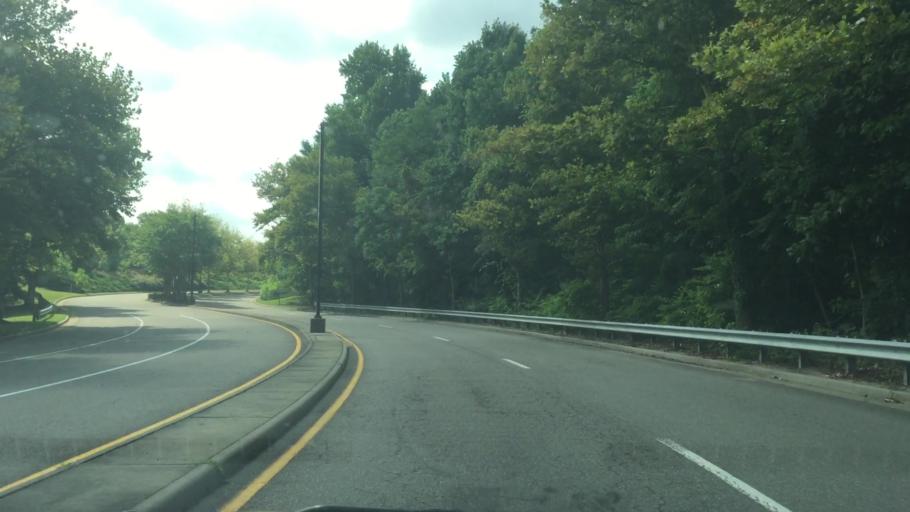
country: US
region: Virginia
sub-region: Henrico County
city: Chamberlayne
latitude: 37.6475
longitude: -77.4048
